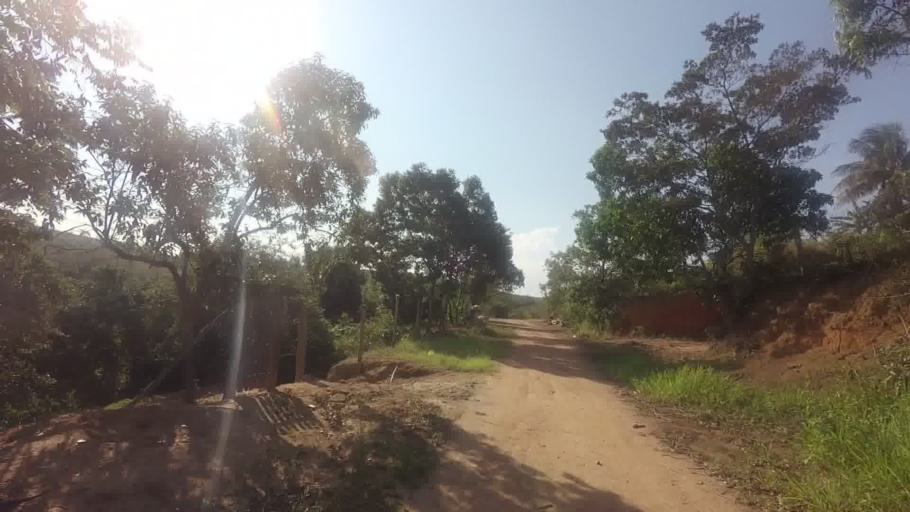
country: BR
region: Espirito Santo
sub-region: Guarapari
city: Guarapari
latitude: -20.7198
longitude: -40.5327
